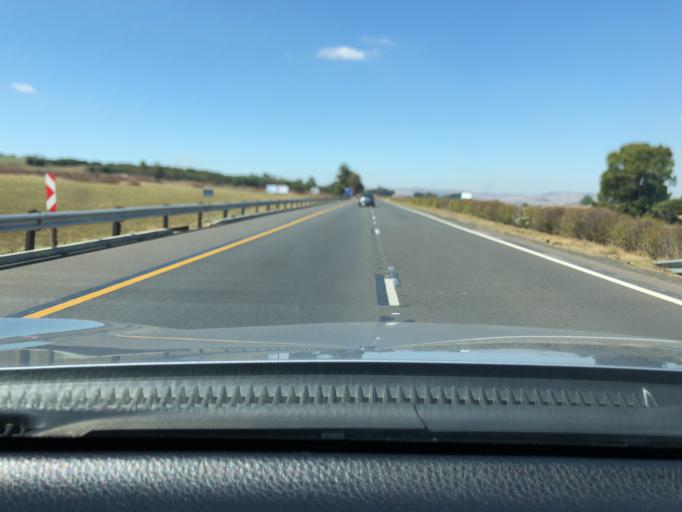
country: ZA
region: KwaZulu-Natal
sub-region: uMgungundlovu District Municipality
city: Mooirivier
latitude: -29.1348
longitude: 29.9609
